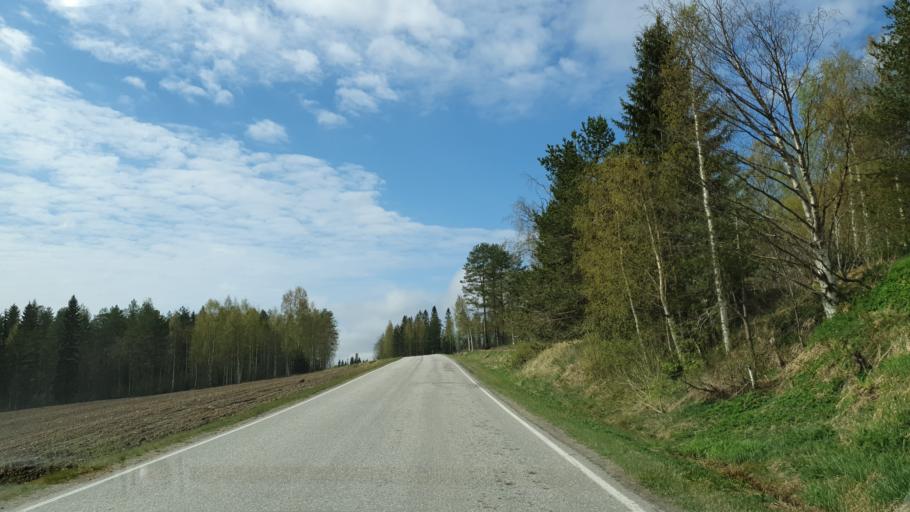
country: FI
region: Kainuu
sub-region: Kehys-Kainuu
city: Kuhmo
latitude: 64.1249
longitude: 29.6477
